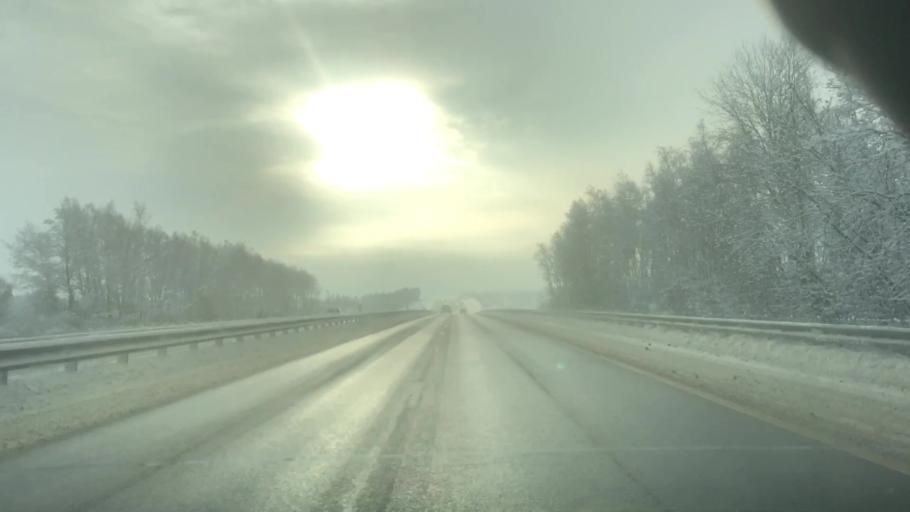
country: RU
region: Tula
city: Venev
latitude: 54.3250
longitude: 38.1545
